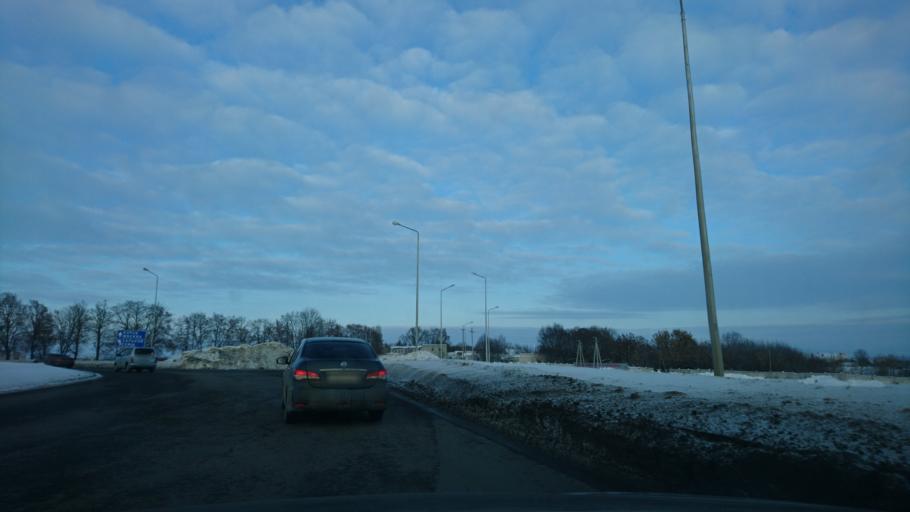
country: RU
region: Belgorod
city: Severnyy
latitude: 50.6603
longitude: 36.5639
